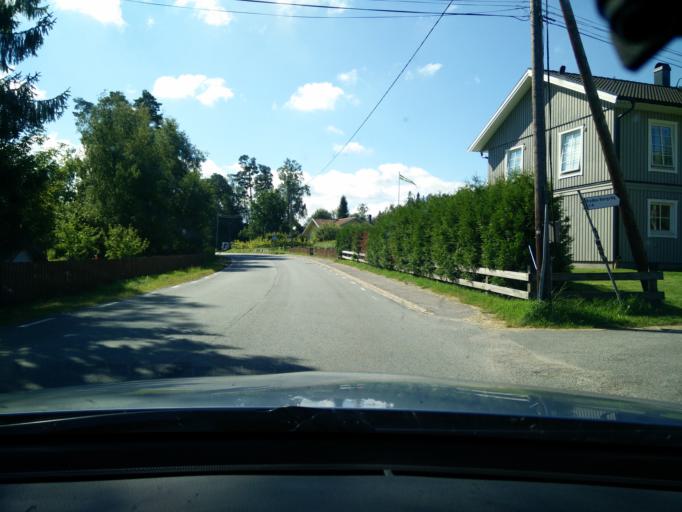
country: SE
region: Stockholm
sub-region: Lidingo
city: Lidingoe
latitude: 59.4643
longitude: 18.1834
